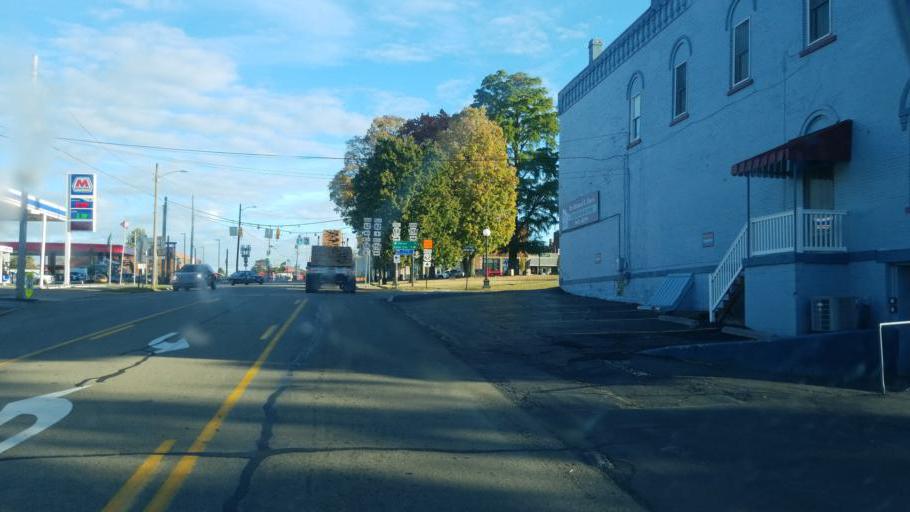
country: US
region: Pennsylvania
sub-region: Mercer County
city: Mercer
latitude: 41.2262
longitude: -80.2399
